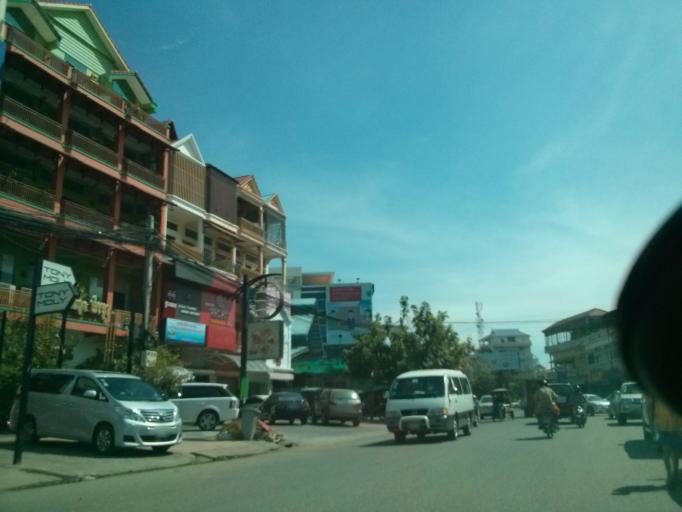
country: KH
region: Phnom Penh
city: Phnom Penh
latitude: 11.5840
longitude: 104.8992
